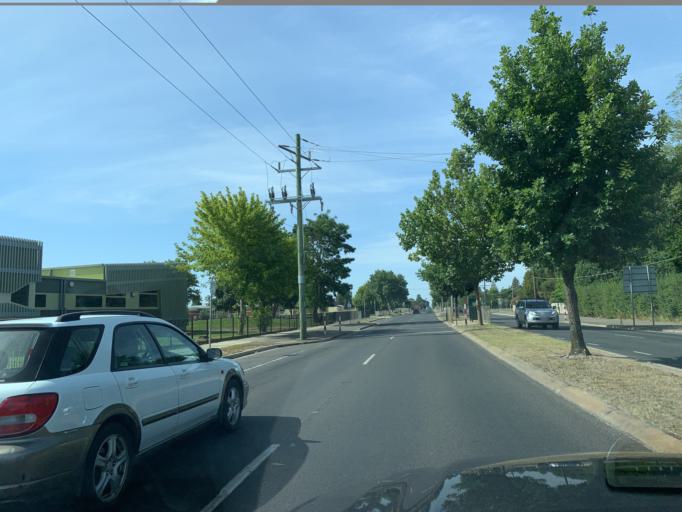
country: AU
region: Victoria
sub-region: Ballarat North
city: Newington
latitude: -37.5547
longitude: 143.8192
